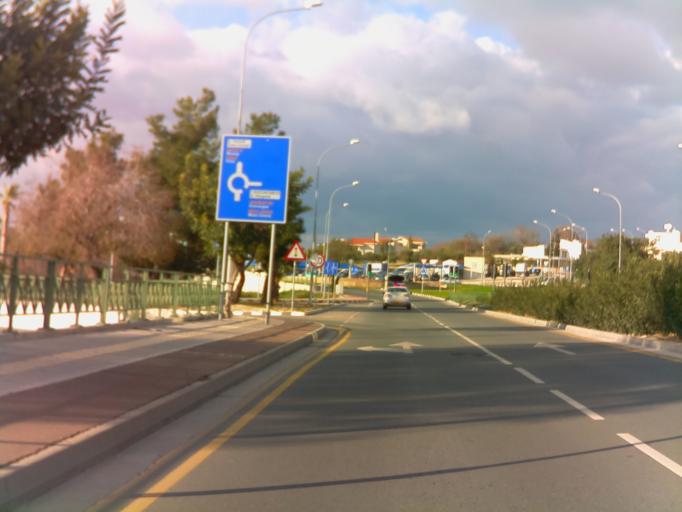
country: CY
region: Pafos
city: Paphos
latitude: 34.7868
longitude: 32.4408
